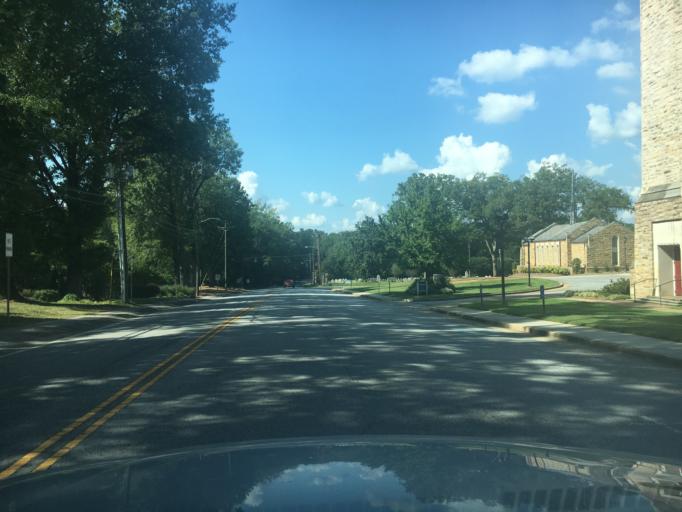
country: US
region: South Carolina
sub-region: Greenwood County
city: Greenwood
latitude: 34.2054
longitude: -82.1633
